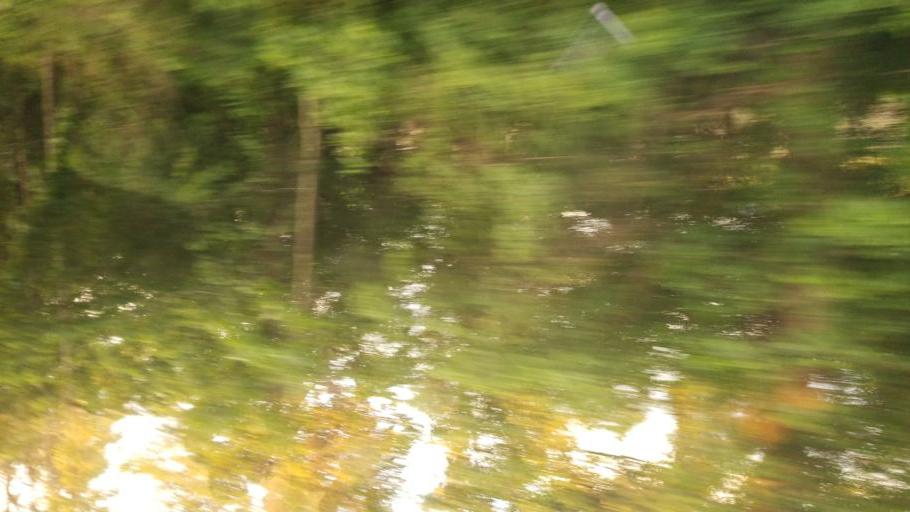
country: US
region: Virginia
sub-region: Culpeper County
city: Culpeper
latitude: 38.4802
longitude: -77.9675
